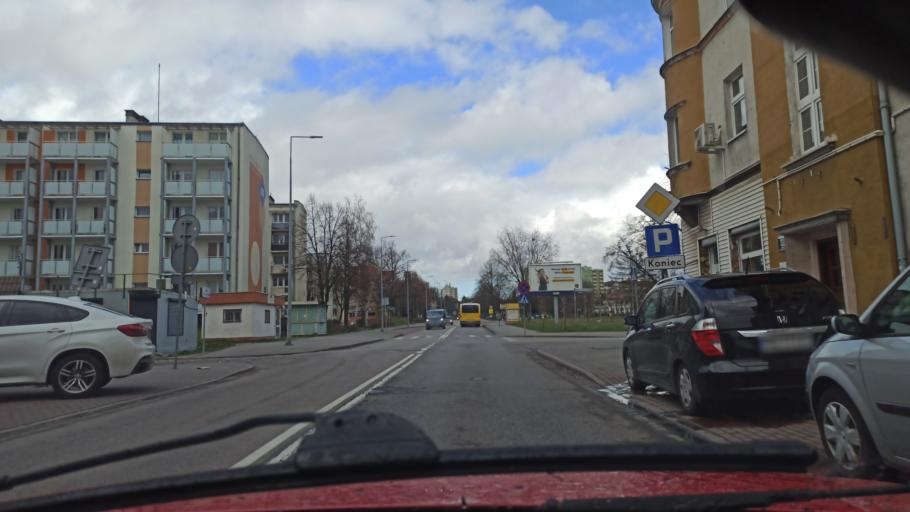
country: PL
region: Warmian-Masurian Voivodeship
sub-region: Powiat elblaski
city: Elblag
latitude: 54.1554
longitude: 19.4166
